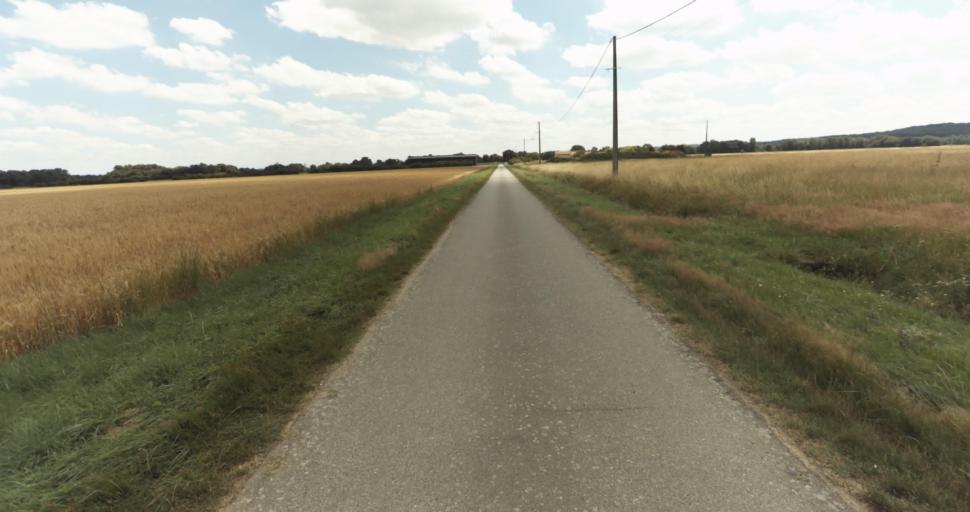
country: FR
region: Midi-Pyrenees
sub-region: Departement de la Haute-Garonne
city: Fontenilles
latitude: 43.5675
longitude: 1.1793
